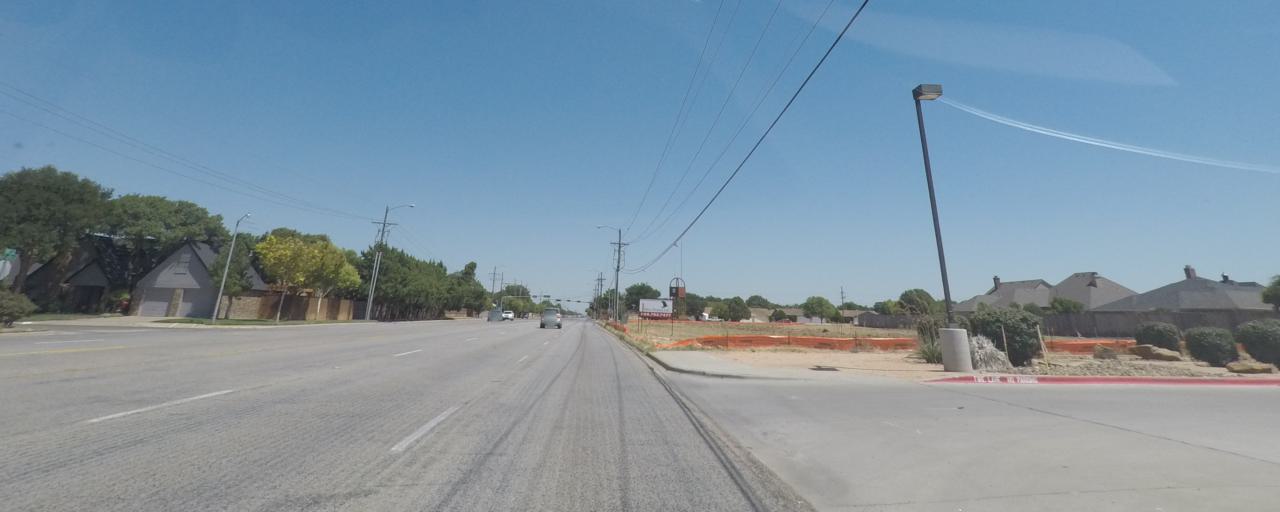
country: US
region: Texas
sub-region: Lubbock County
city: Lubbock
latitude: 33.5052
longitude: -101.8990
